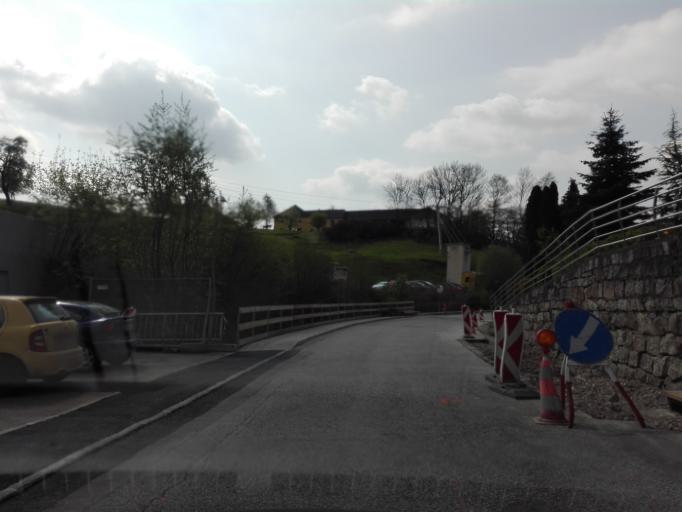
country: AT
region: Upper Austria
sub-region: Politischer Bezirk Perg
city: Perg
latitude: 48.2332
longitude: 14.7056
